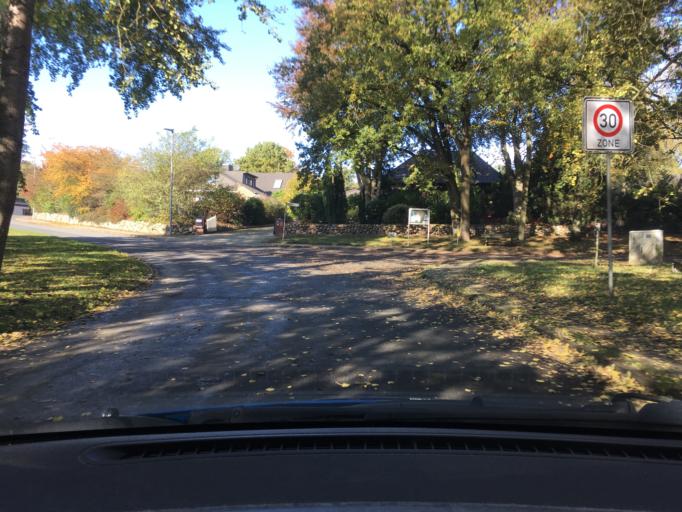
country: DE
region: Lower Saxony
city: Kakenstorf
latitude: 53.3096
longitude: 9.7886
